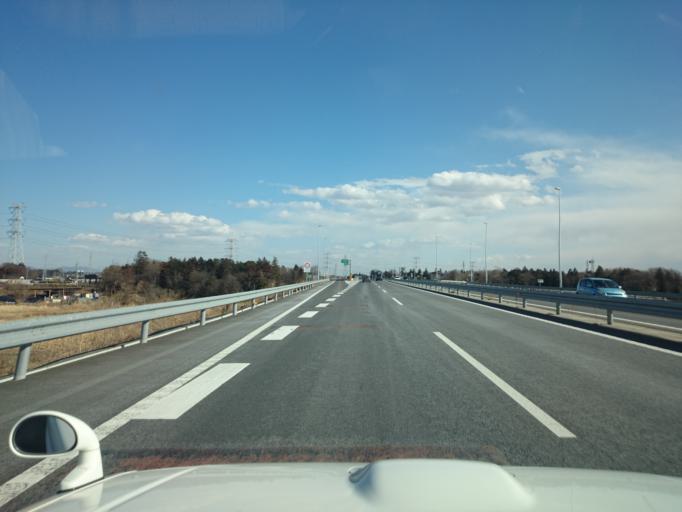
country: JP
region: Ibaraki
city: Sakai
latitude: 36.1261
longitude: 139.8043
